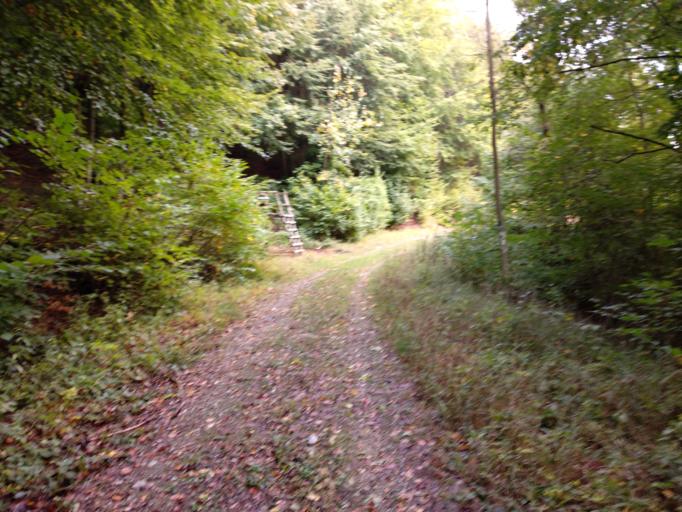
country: DE
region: North Rhine-Westphalia
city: Beverungen
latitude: 51.6411
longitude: 9.3634
